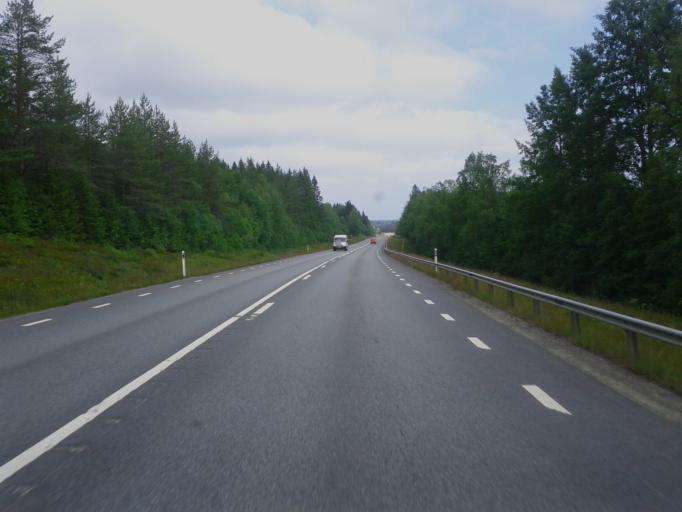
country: SE
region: Vaesterbotten
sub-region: Skelleftea Kommun
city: Burea
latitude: 64.3610
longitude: 21.2964
